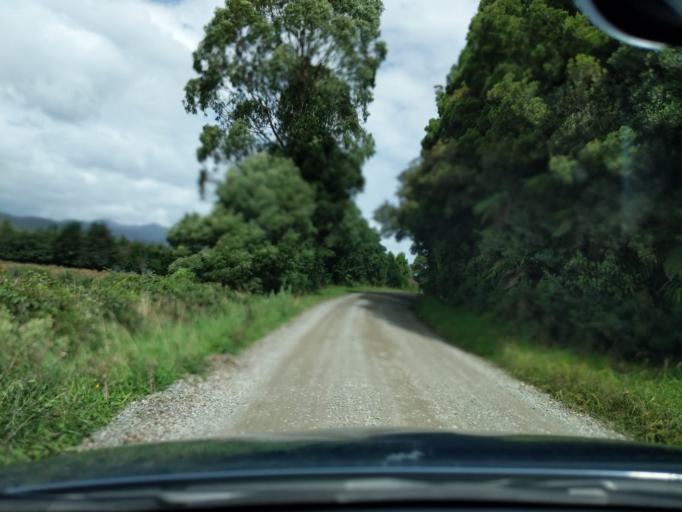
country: NZ
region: Tasman
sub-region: Tasman District
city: Takaka
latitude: -40.6493
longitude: 172.4695
